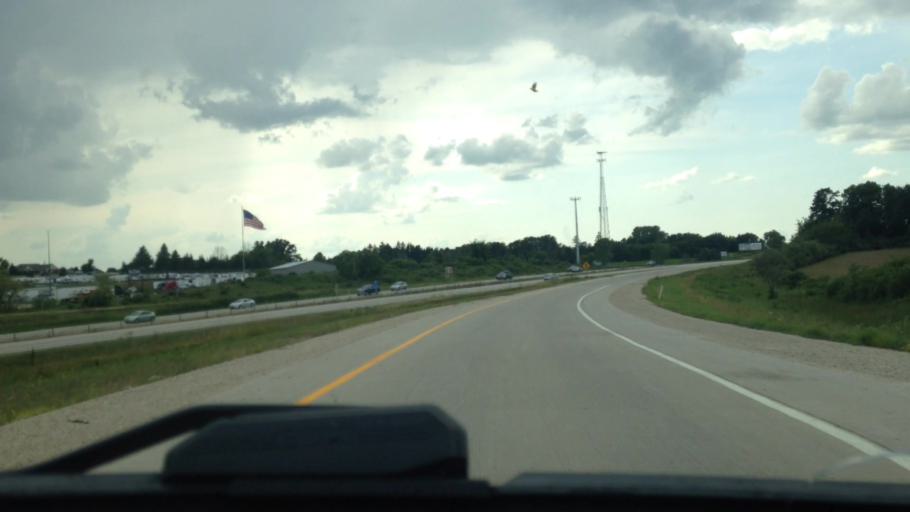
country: US
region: Wisconsin
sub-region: Washington County
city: Richfield
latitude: 43.2831
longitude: -88.1942
